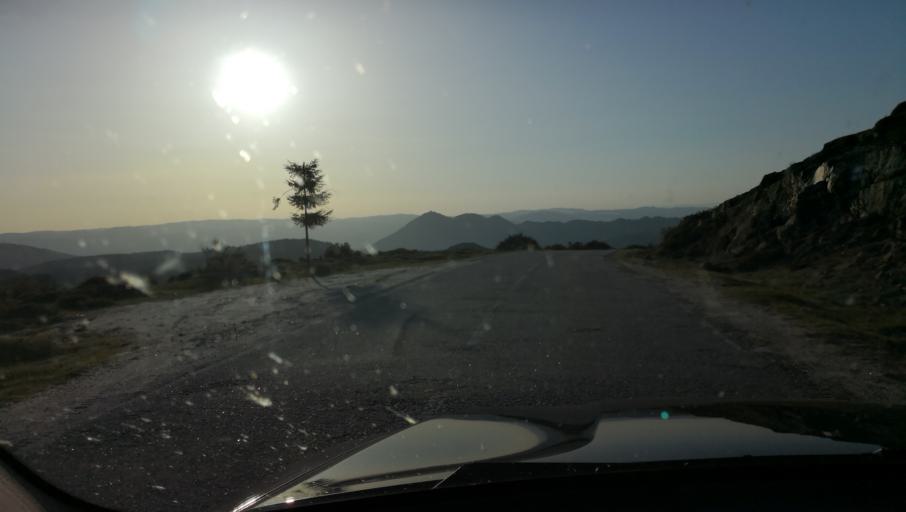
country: PT
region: Vila Real
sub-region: Vila Real
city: Vila Real
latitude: 41.3813
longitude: -7.8206
